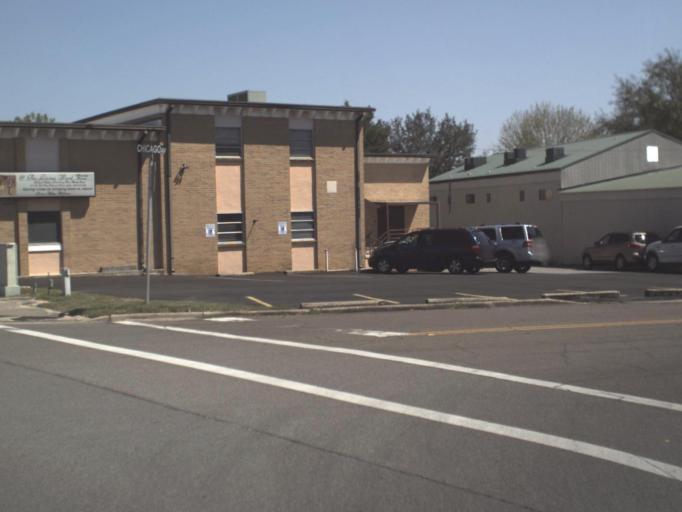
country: US
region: Florida
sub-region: Okaloosa County
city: Valparaiso
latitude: 30.5118
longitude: -86.4937
